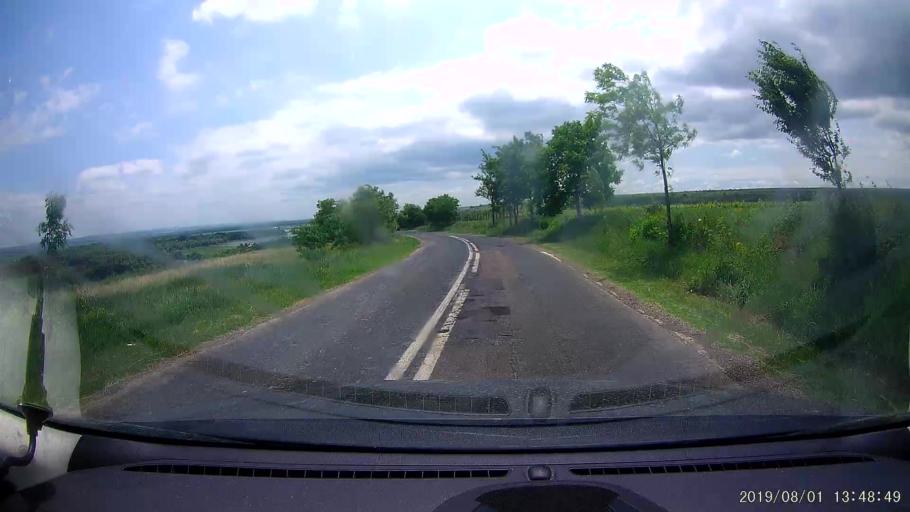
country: RO
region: Galati
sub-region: Comuna Oancea
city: Oancea
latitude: 45.9023
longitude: 28.1096
